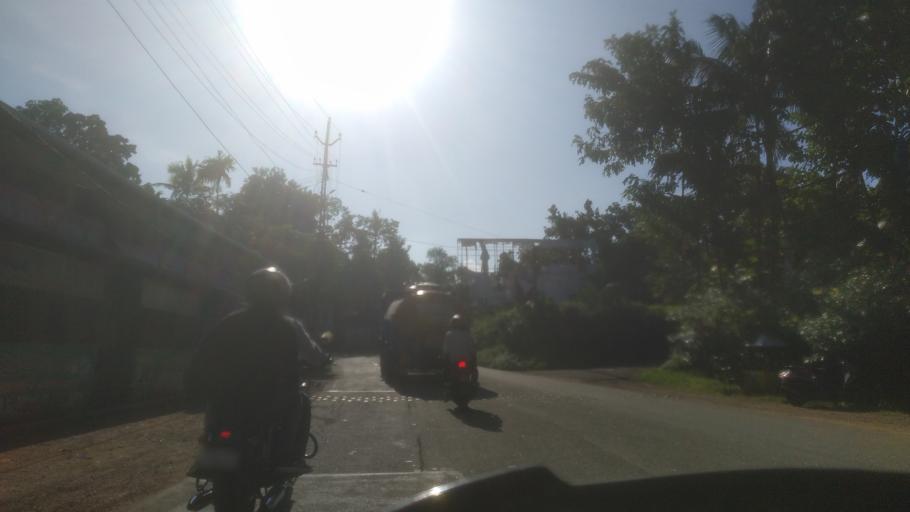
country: IN
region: Kerala
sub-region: Ernakulam
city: Ramamangalam
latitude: 9.9746
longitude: 76.5011
